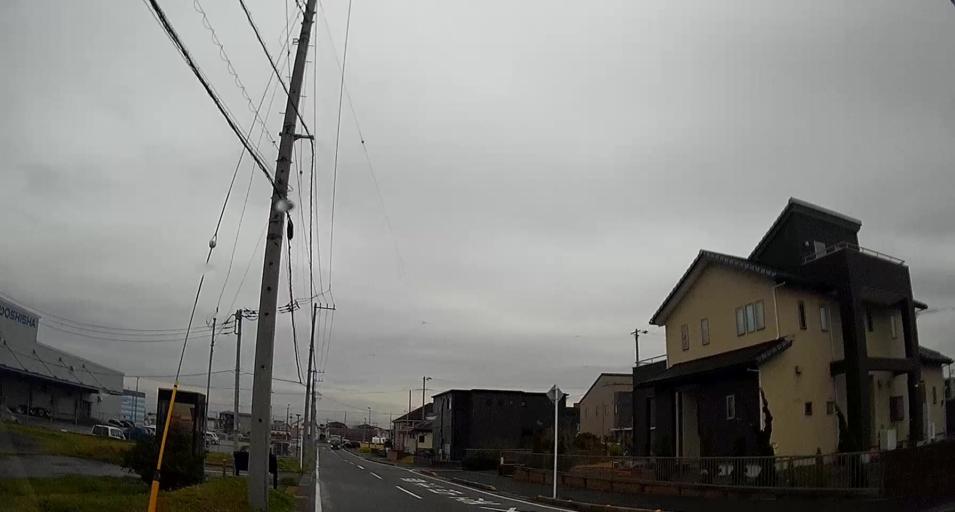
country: JP
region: Chiba
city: Kisarazu
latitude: 35.4396
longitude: 139.9277
